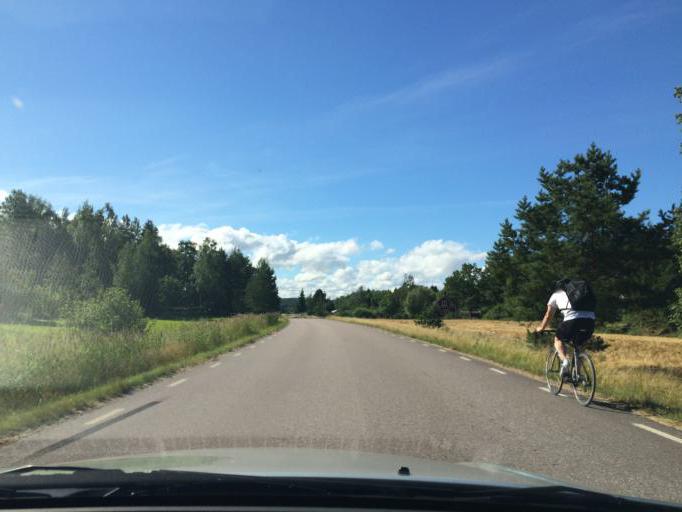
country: SE
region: Soedermanland
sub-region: Eskilstuna Kommun
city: Torshalla
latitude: 59.5211
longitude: 16.4379
